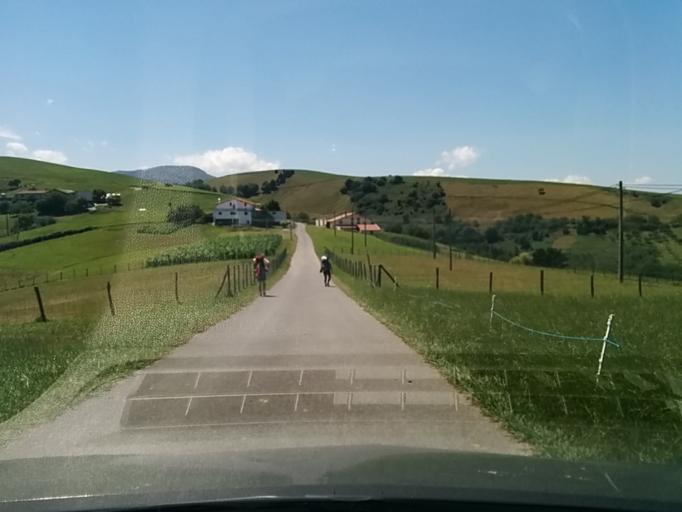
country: ES
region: Basque Country
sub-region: Provincia de Guipuzcoa
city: Zumaia
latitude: 43.2921
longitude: -2.2694
